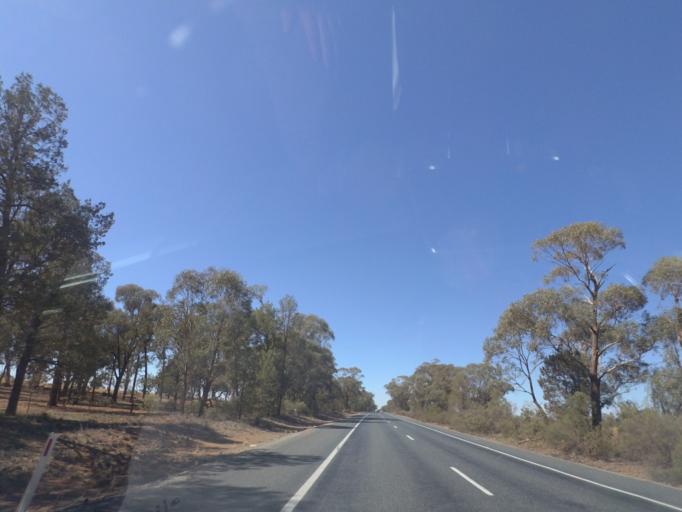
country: AU
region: New South Wales
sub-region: Bland
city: West Wyalong
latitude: -34.2107
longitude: 147.1088
